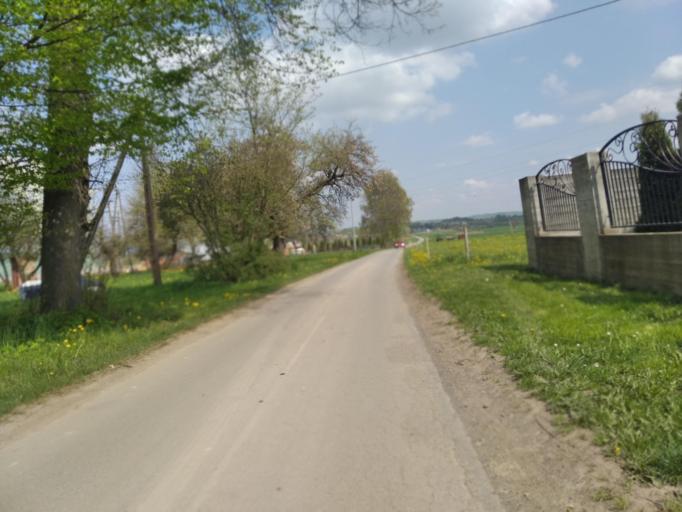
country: PL
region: Subcarpathian Voivodeship
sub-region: Powiat brzozowski
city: Turze Pole
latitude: 49.6451
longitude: 22.0132
